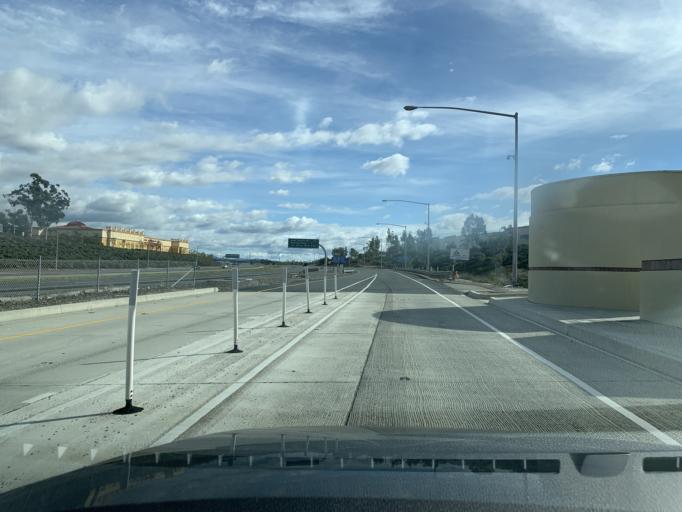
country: US
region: California
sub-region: Orange County
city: Foothill Ranch
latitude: 33.6779
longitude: -117.6726
